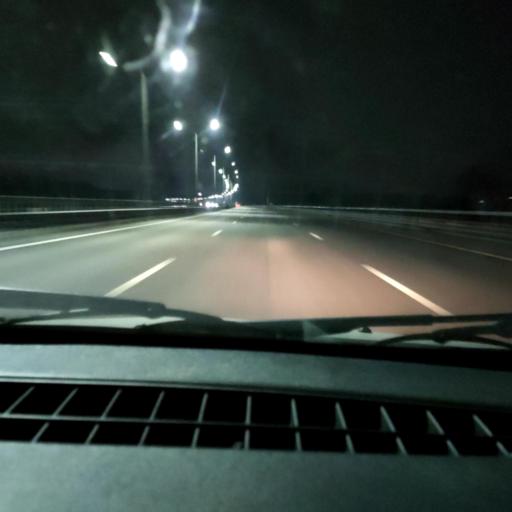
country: RU
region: Voronezj
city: Somovo
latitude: 51.7851
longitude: 39.2880
